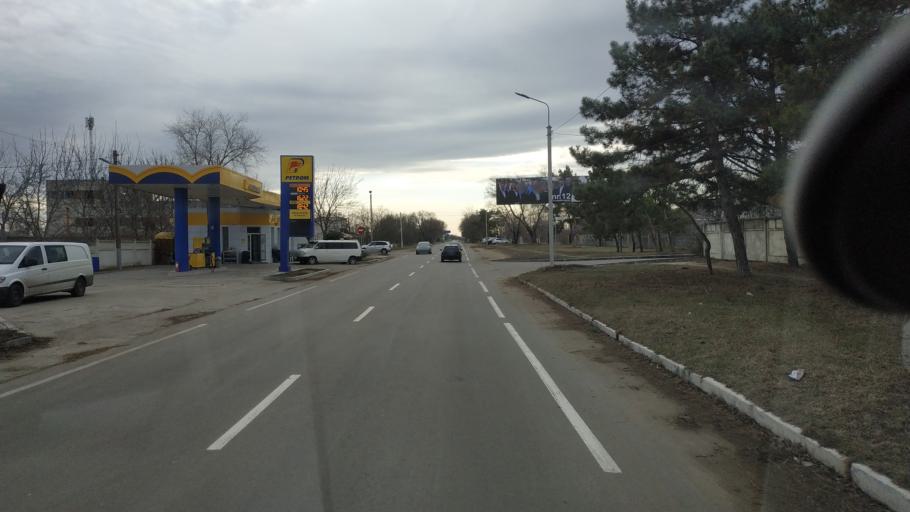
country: MD
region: Criuleni
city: Criuleni
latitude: 47.2033
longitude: 29.1556
